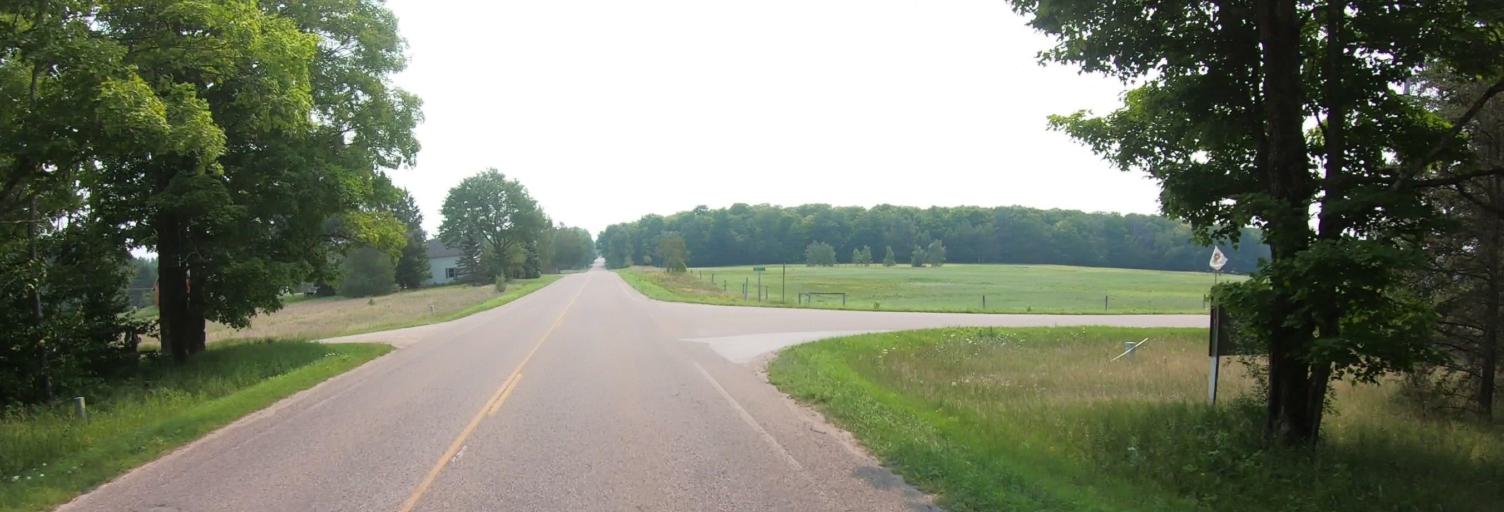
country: CA
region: Ontario
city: Thessalon
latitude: 46.0062
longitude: -83.7385
